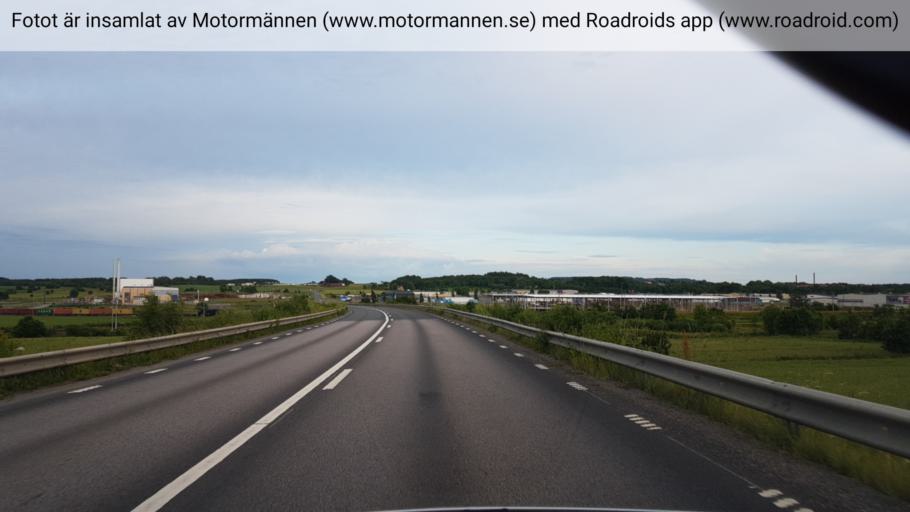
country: SE
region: Vaestra Goetaland
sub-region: Falkopings Kommun
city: Falkoeping
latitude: 58.1882
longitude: 13.5627
